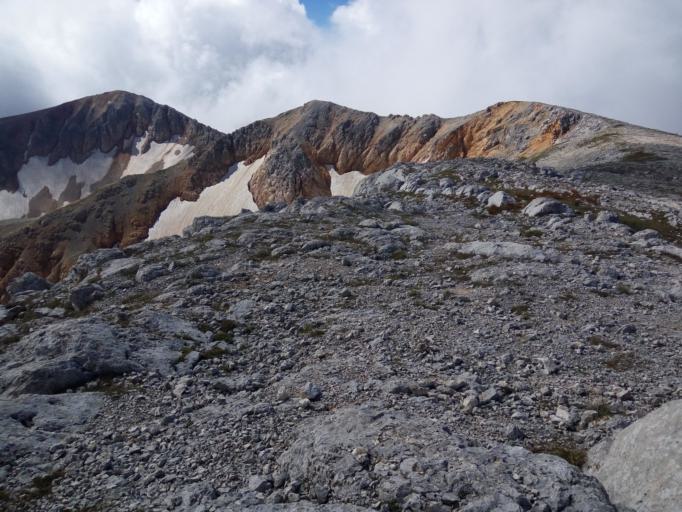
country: RU
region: Adygeya
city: Kamennomostskiy
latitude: 43.9970
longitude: 39.9294
